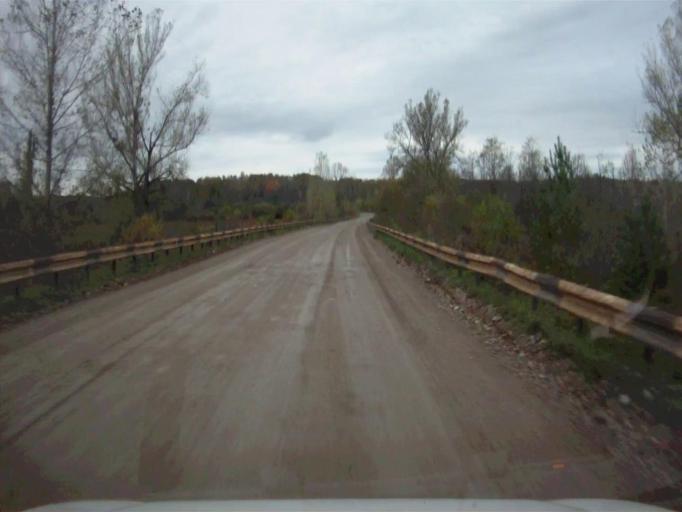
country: RU
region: Chelyabinsk
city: Nyazepetrovsk
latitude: 56.1317
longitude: 59.3212
